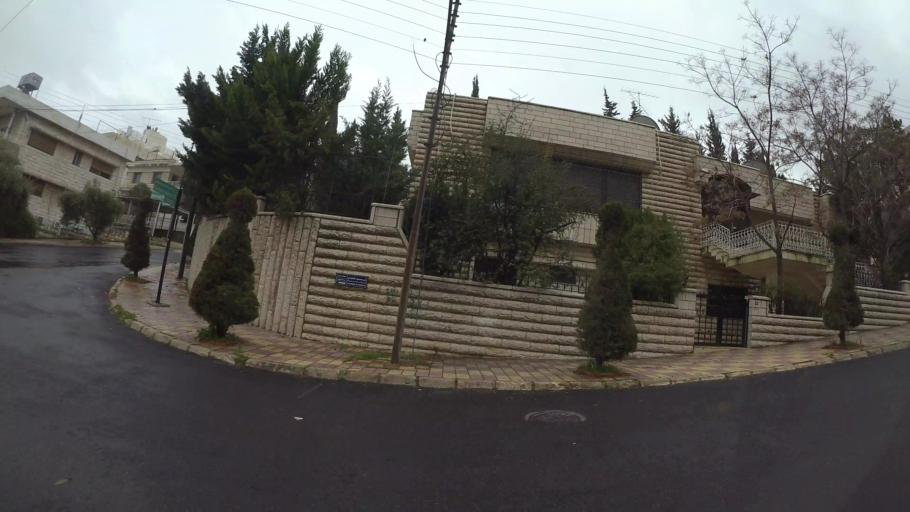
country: JO
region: Amman
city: Amman
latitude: 31.9581
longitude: 35.9019
